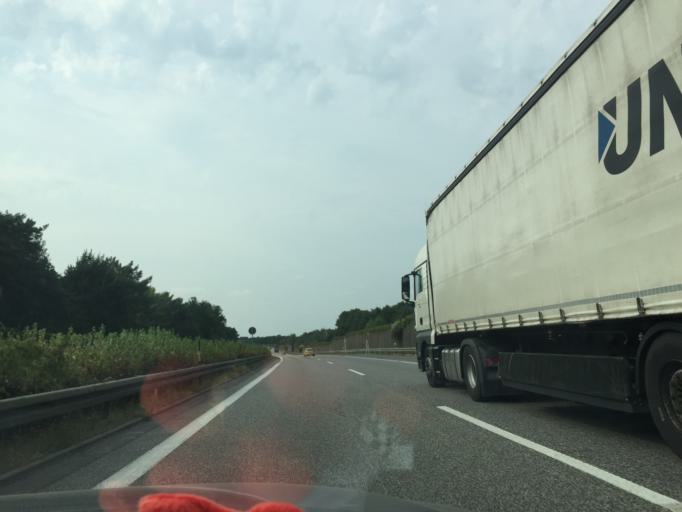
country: DE
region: Brandenburg
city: Schwerin
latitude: 52.1595
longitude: 13.6467
